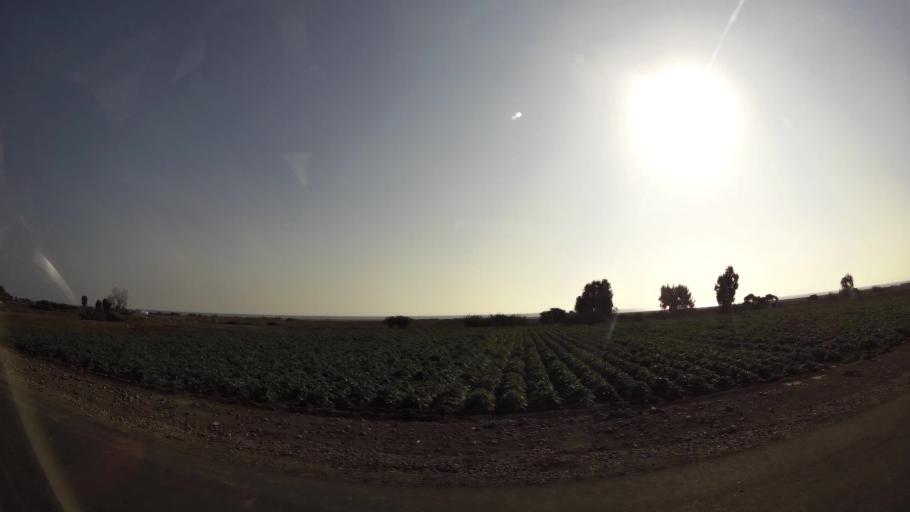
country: PE
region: Ica
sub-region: Provincia de Chincha
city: Chincha Baja
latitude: -13.5351
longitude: -76.1832
